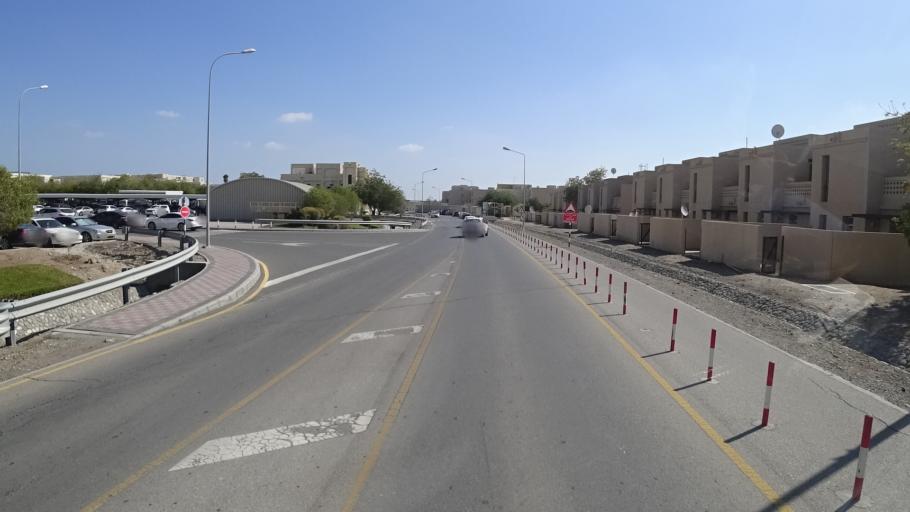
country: OM
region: Muhafazat Masqat
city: As Sib al Jadidah
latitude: 23.5858
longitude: 58.1677
